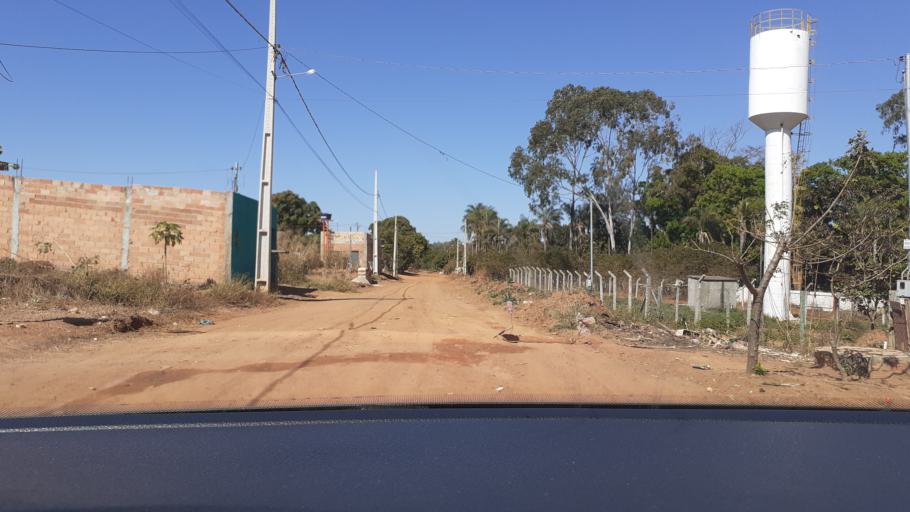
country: BR
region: Goias
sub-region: Aparecida De Goiania
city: Aparecida de Goiania
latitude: -16.8811
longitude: -49.2609
